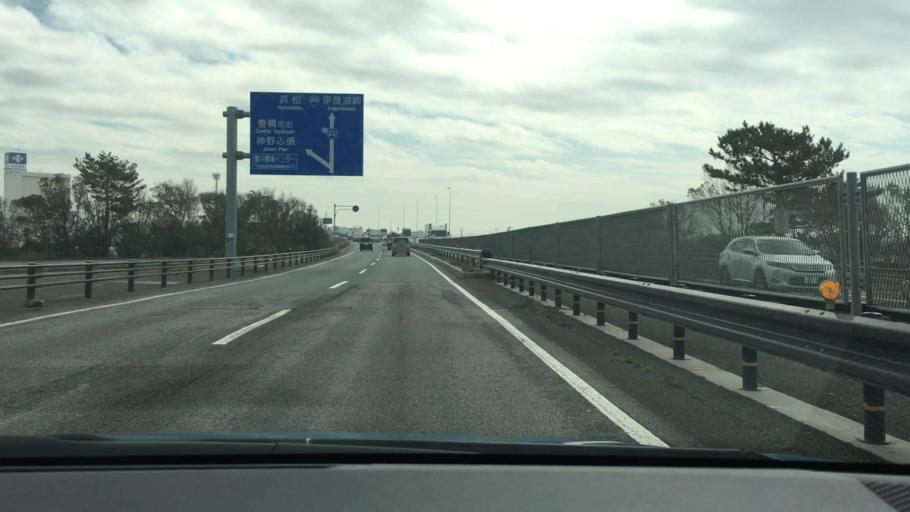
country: JP
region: Aichi
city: Kozakai-cho
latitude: 34.7668
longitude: 137.3322
